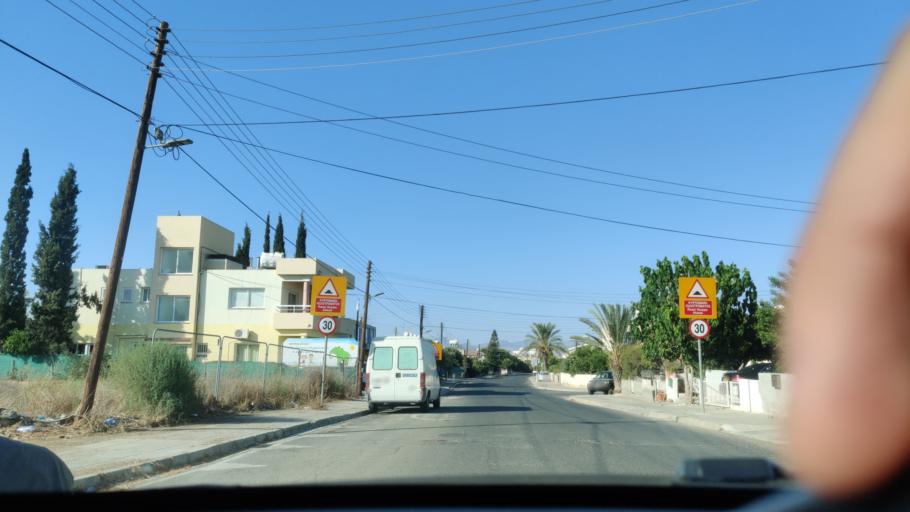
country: CY
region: Lefkosia
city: Tseri
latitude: 35.1144
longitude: 33.3240
